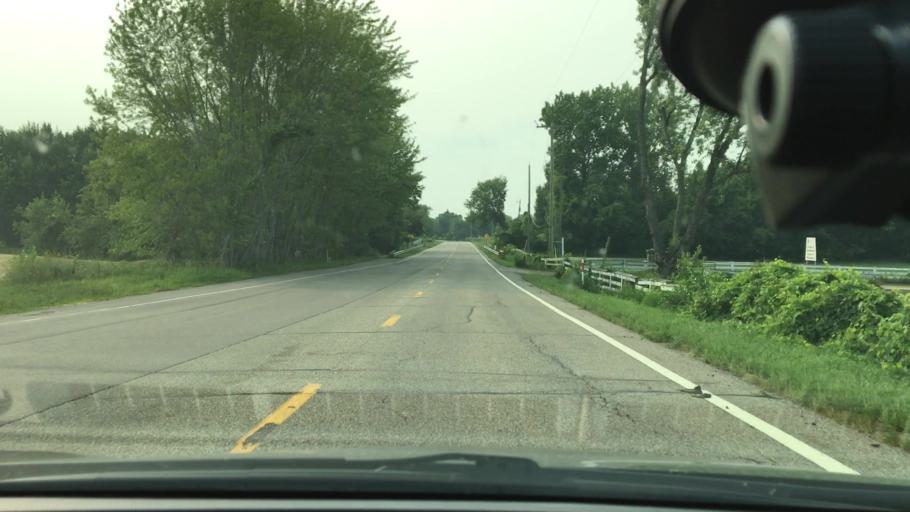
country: US
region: Minnesota
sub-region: Anoka County
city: Ramsey
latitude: 45.2222
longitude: -93.4653
